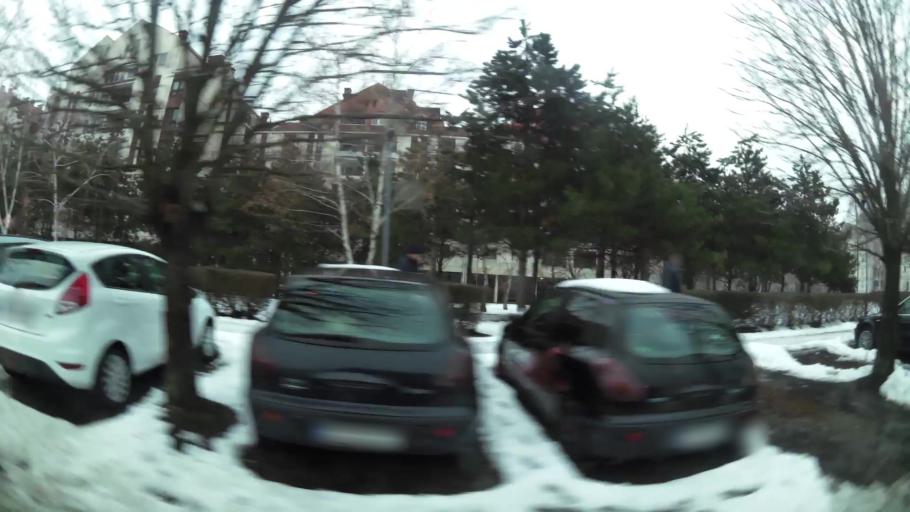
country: RS
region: Central Serbia
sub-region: Belgrade
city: Zemun
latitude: 44.8165
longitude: 20.3796
